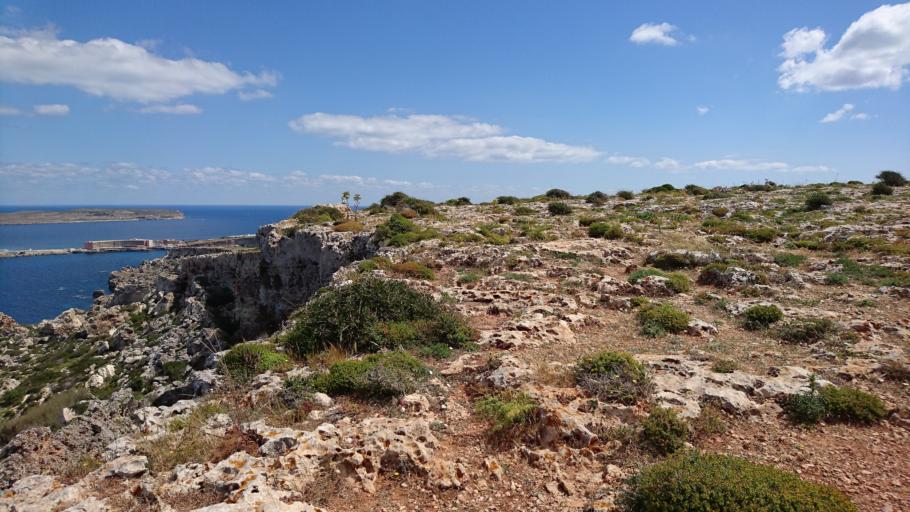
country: MT
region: Il-Mellieha
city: Mellieha
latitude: 35.9730
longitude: 14.3242
